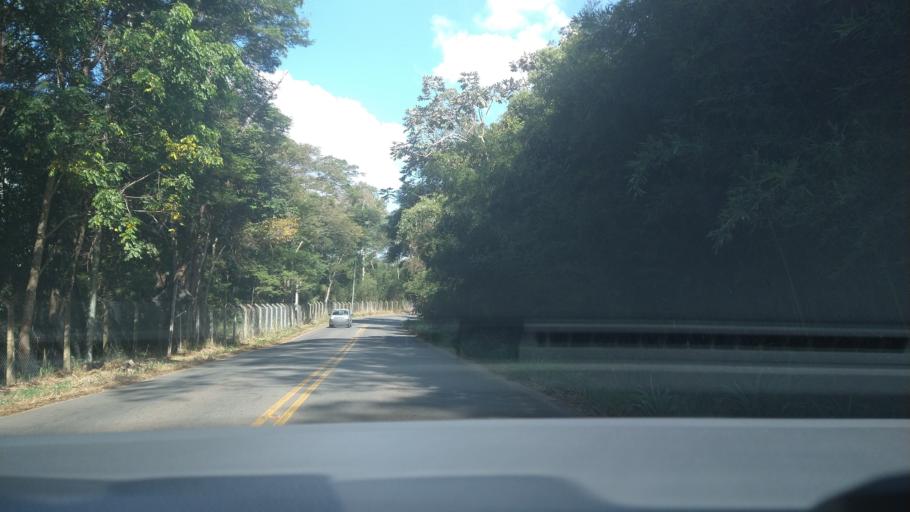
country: BR
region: Minas Gerais
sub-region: Vicosa
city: Vicosa
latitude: -20.7645
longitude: -42.8710
